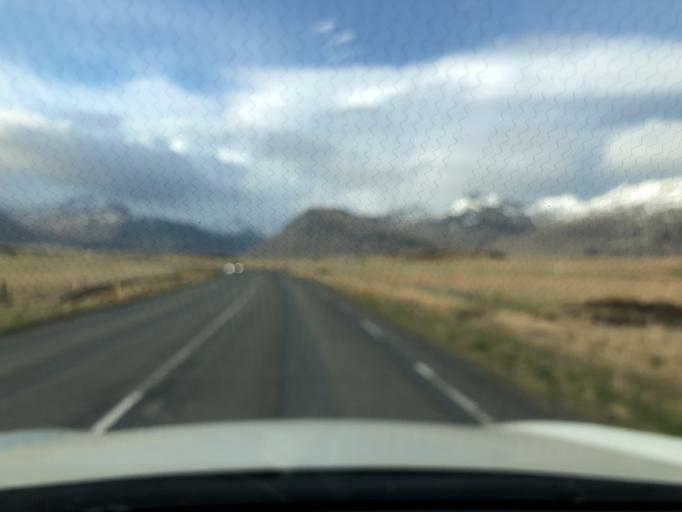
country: IS
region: East
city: Hoefn
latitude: 64.2881
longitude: -15.1830
